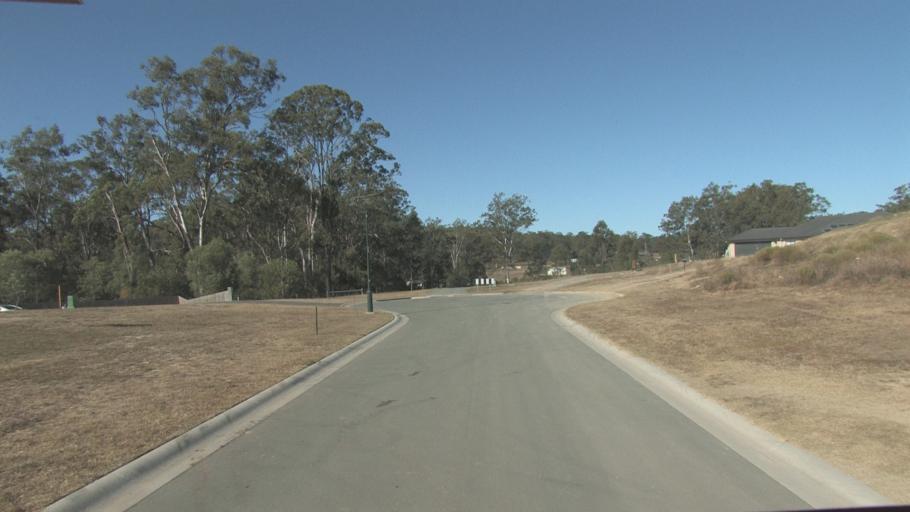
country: AU
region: Queensland
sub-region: Logan
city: Cedar Vale
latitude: -27.8640
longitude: 153.0544
